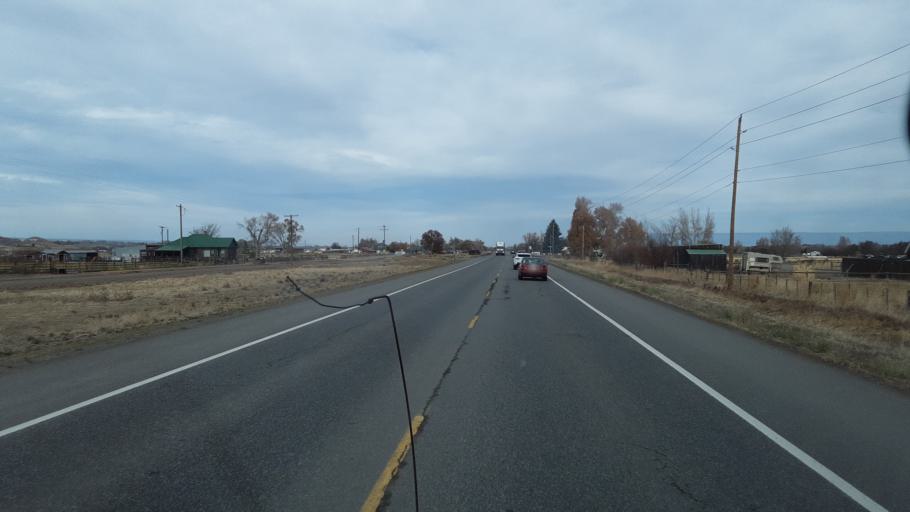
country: US
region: Colorado
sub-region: Montrose County
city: Montrose
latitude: 38.3985
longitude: -107.8365
